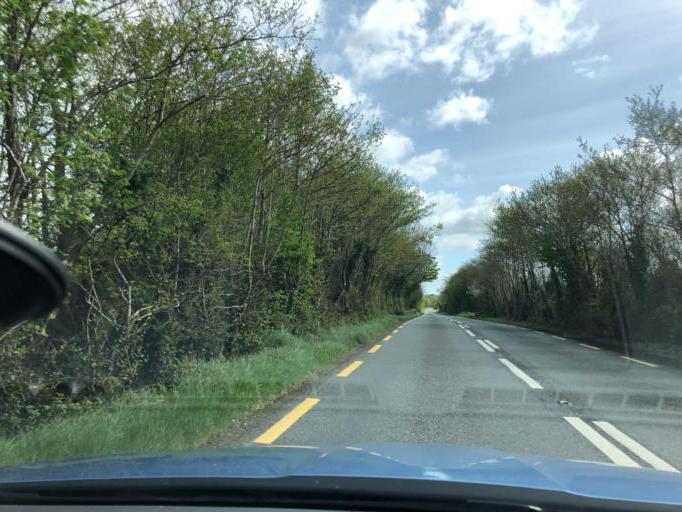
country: IE
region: Munster
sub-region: Ciarrai
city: Cill Airne
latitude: 52.0584
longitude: -9.3569
